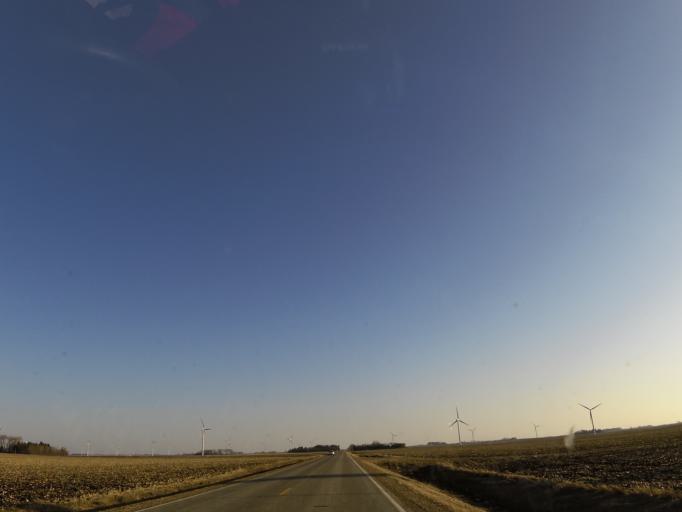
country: US
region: Iowa
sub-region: Worth County
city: Northwood
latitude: 43.4225
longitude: -93.1244
